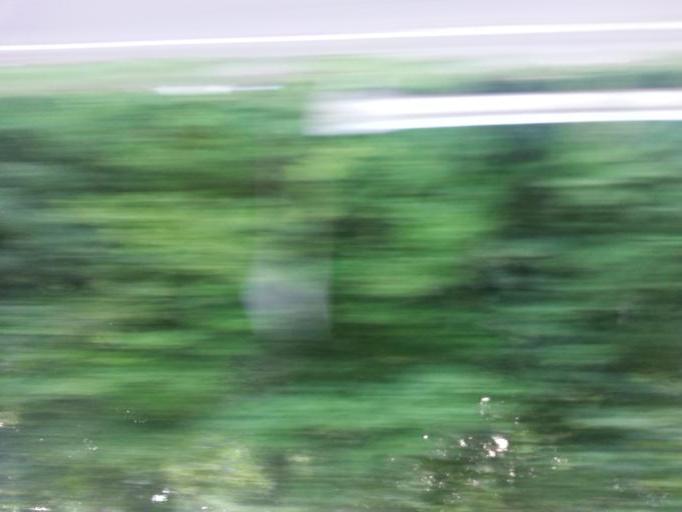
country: US
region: Tennessee
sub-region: McMinn County
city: Athens
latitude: 35.4585
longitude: -84.5810
